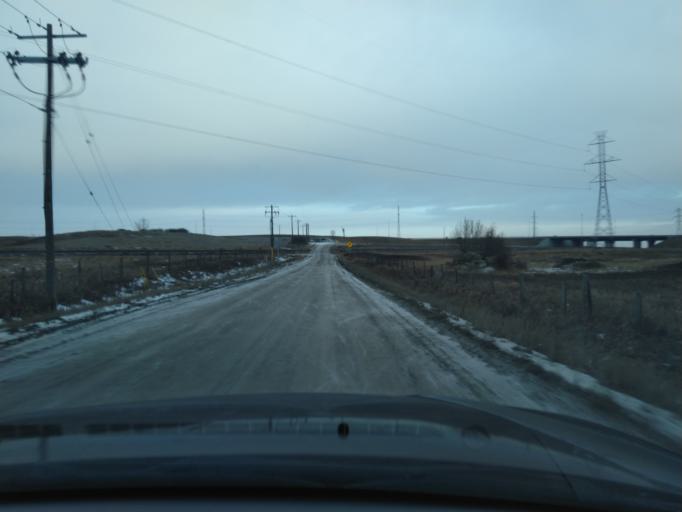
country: CA
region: Alberta
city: Airdrie
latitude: 51.1713
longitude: -114.0249
